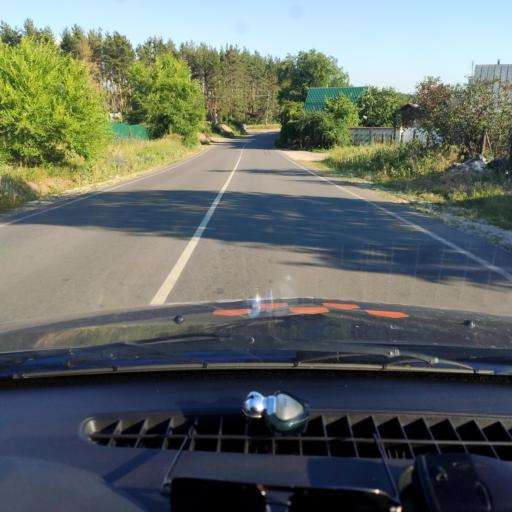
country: RU
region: Voronezj
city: Podgornoye
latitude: 51.8387
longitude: 39.1434
